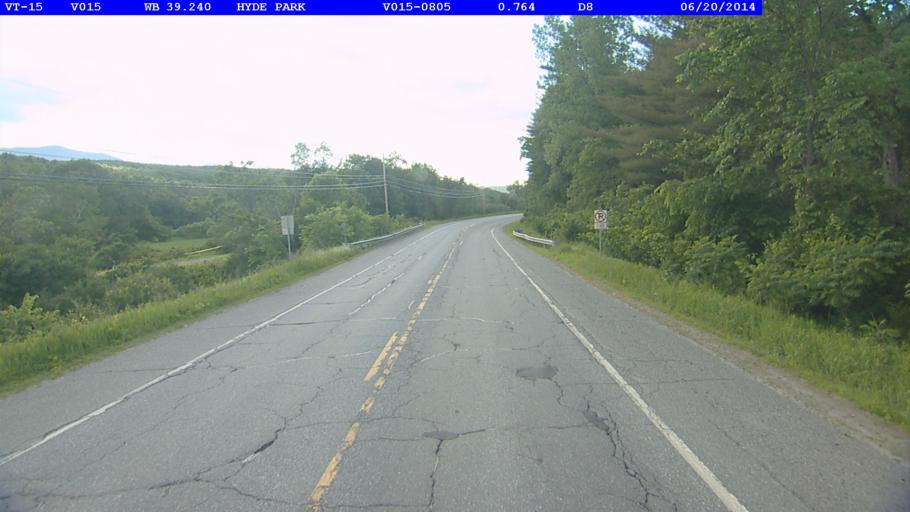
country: US
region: Vermont
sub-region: Lamoille County
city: Hyde Park
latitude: 44.6013
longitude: -72.6366
